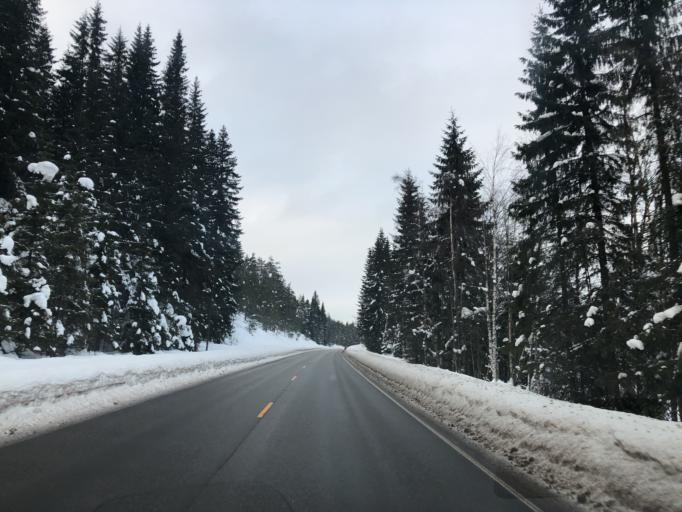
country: NO
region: Hedmark
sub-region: Trysil
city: Innbygda
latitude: 61.2769
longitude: 12.2879
